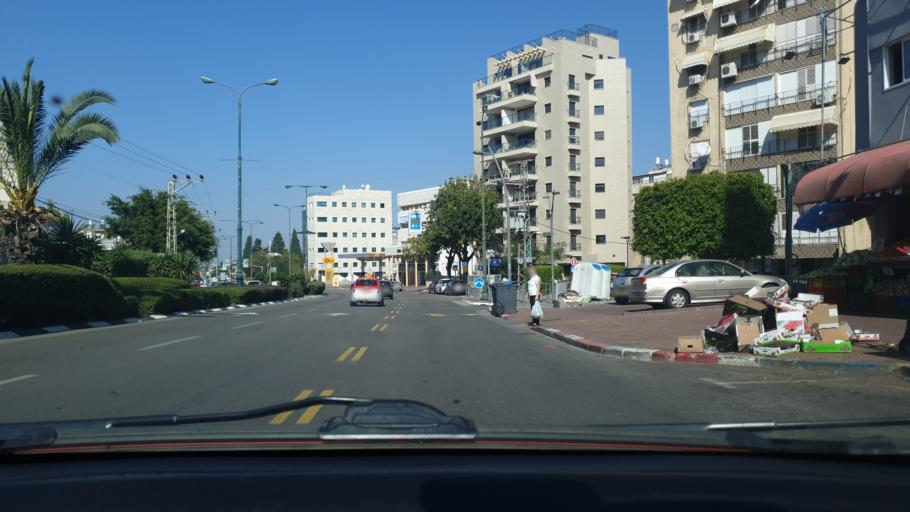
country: IL
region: Central District
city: Rishon LeZiyyon
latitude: 31.9708
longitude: 34.8059
